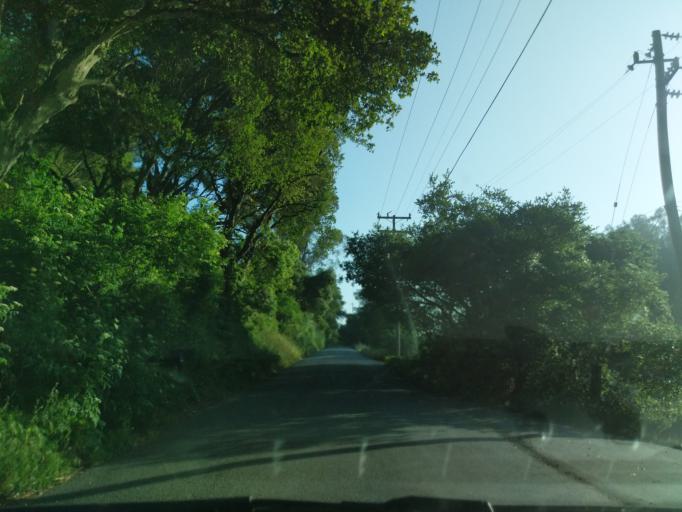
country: US
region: California
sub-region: Monterey County
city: Las Lomas
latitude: 36.8880
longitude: -121.7222
